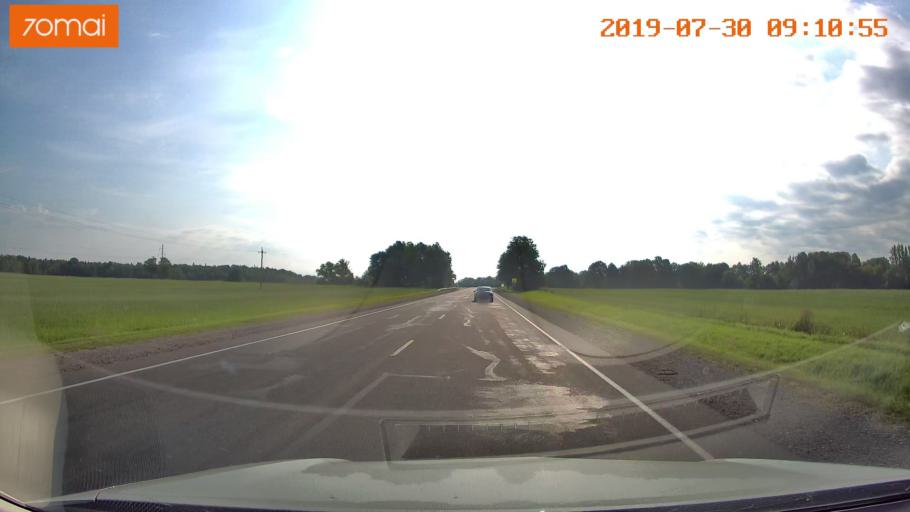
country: RU
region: Kaliningrad
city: Nesterov
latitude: 54.6119
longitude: 22.4391
